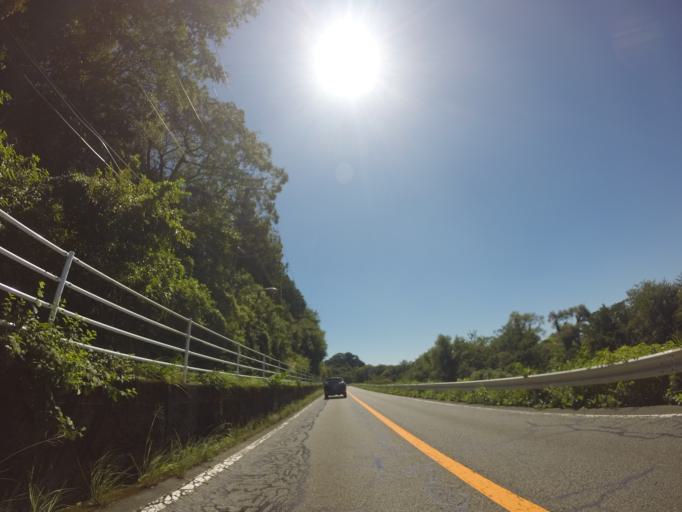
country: JP
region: Shizuoka
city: Kanaya
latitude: 34.8470
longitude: 138.1442
